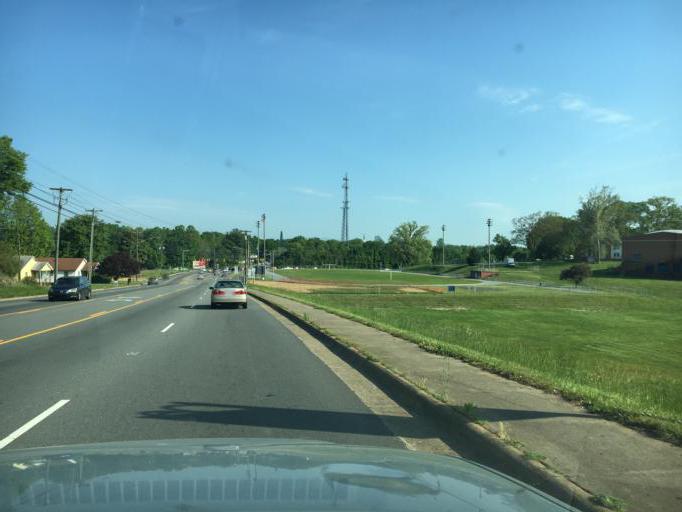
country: US
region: North Carolina
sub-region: Burke County
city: Morganton
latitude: 35.7267
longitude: -81.6927
